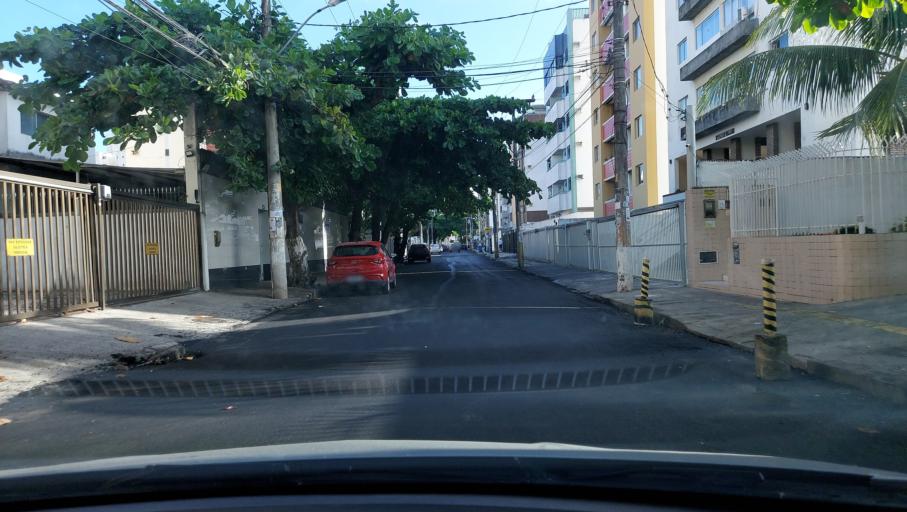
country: BR
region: Bahia
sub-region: Salvador
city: Salvador
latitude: -12.9917
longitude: -38.4472
